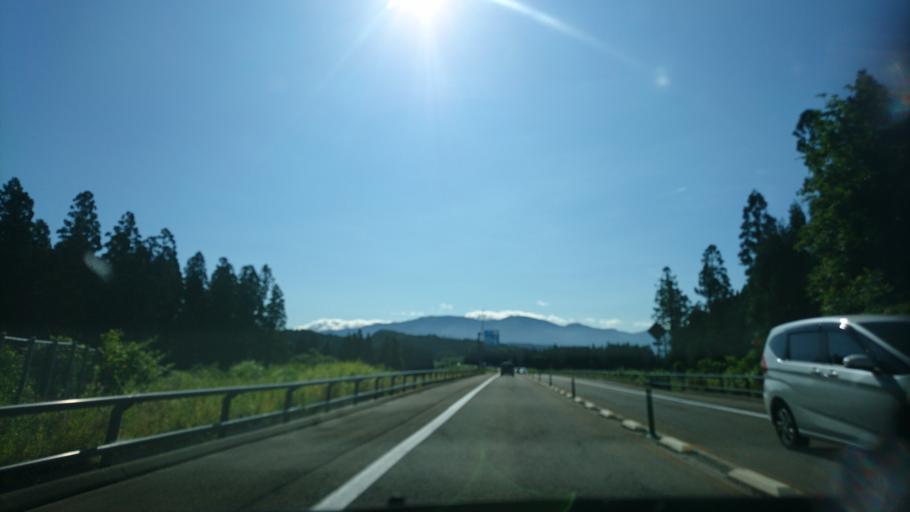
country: JP
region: Akita
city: Kakunodatemachi
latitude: 39.5951
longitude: 140.5342
